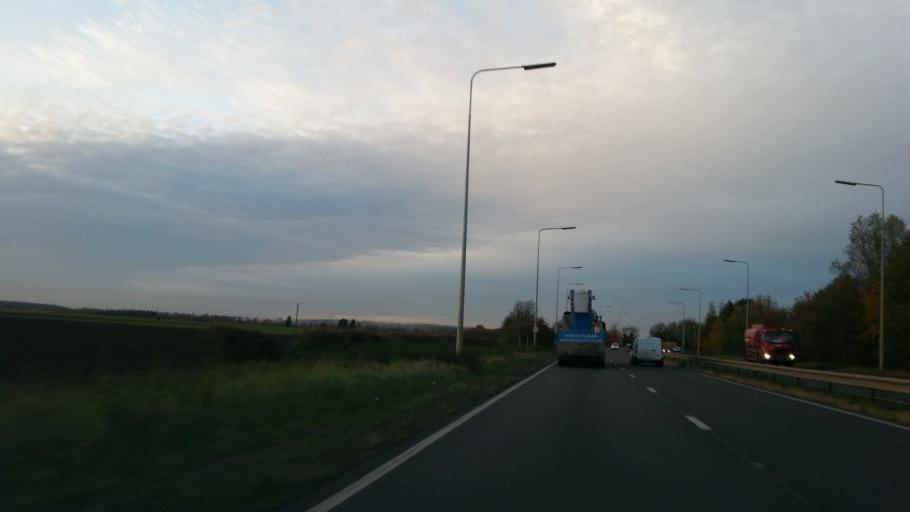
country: GB
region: England
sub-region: Central Bedfordshire
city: Sandy
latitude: 52.1072
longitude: -0.2805
